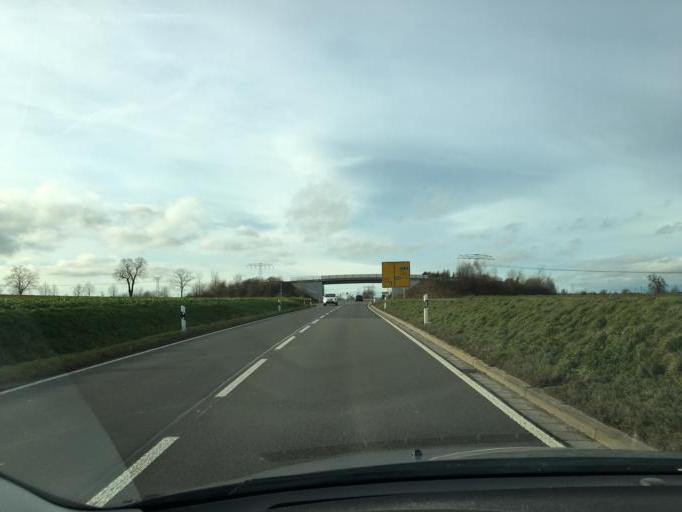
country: DE
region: Thuringia
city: Windischleuba
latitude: 51.0210
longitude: 12.4613
